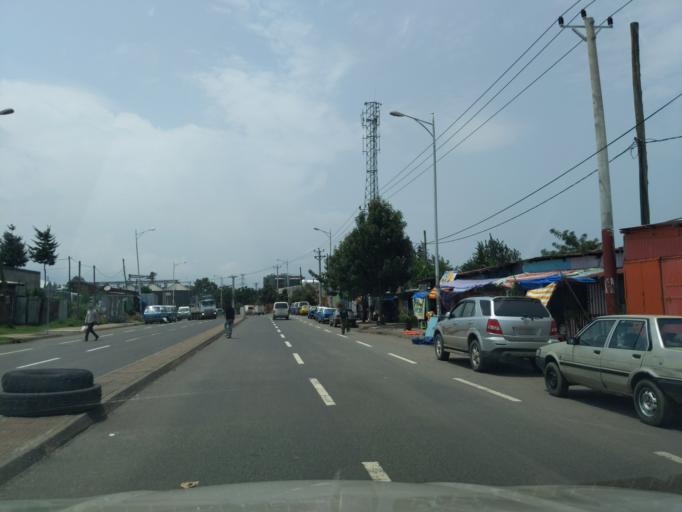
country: ET
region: Adis Abeba
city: Addis Ababa
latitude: 8.9450
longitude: 38.7569
